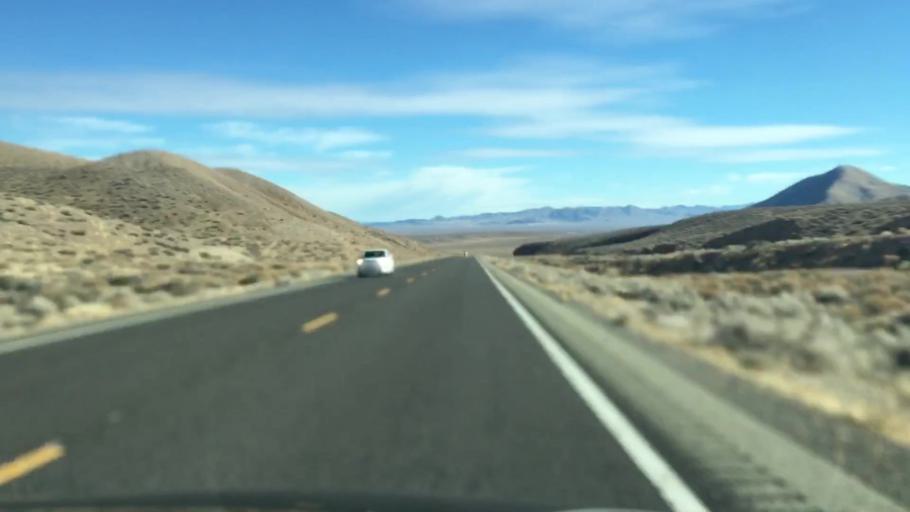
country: US
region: Nevada
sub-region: Lyon County
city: Yerington
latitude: 39.0384
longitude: -118.9343
